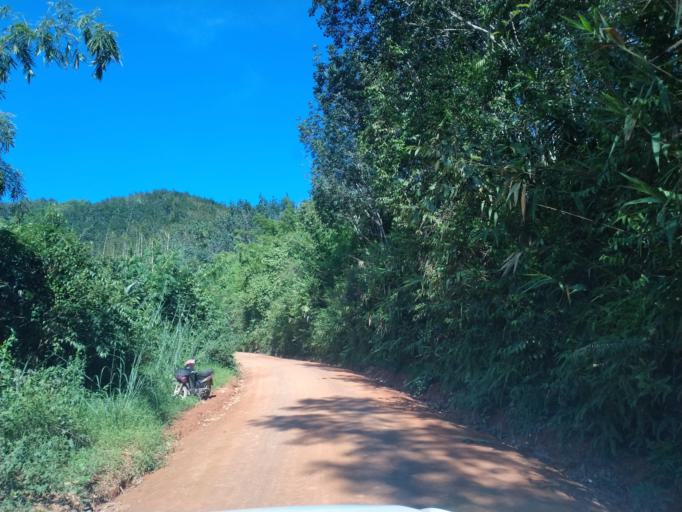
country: TH
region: Changwat Bueng Kan
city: Pak Khat
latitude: 18.6310
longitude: 103.0702
